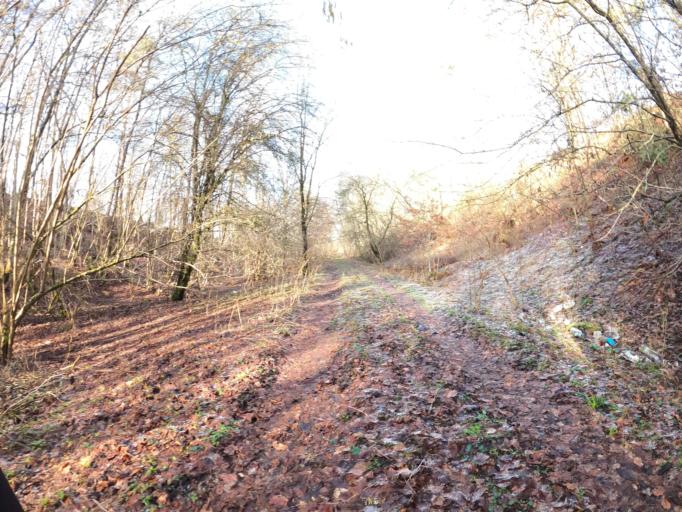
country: PL
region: West Pomeranian Voivodeship
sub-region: Powiat koszalinski
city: Polanow
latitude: 54.1405
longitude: 16.7705
